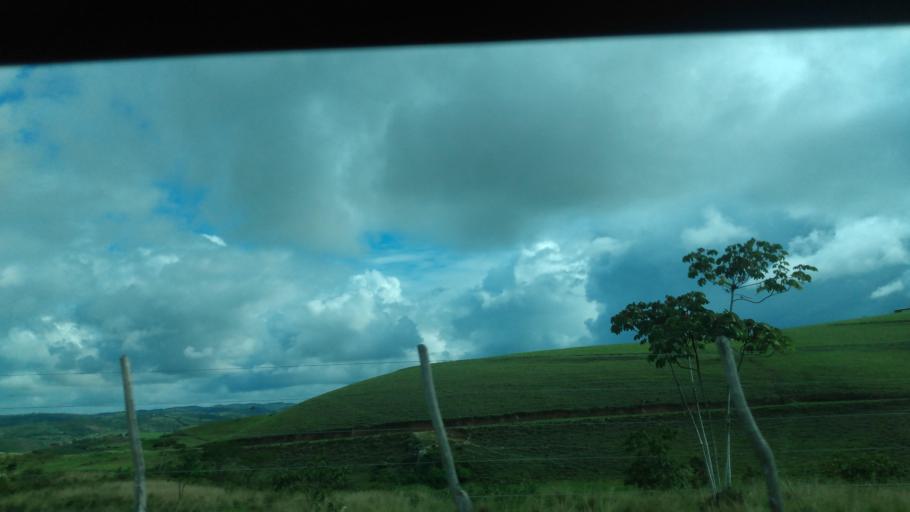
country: BR
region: Pernambuco
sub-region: Quipapa
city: Quipapa
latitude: -8.7799
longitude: -35.9176
